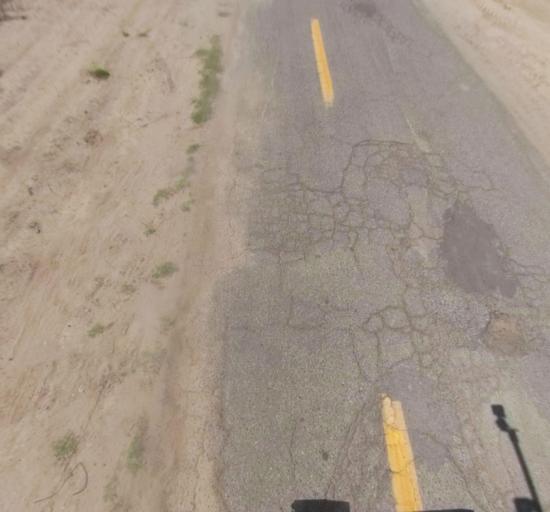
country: US
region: California
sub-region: Madera County
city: Madera
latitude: 36.9598
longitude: -120.1659
